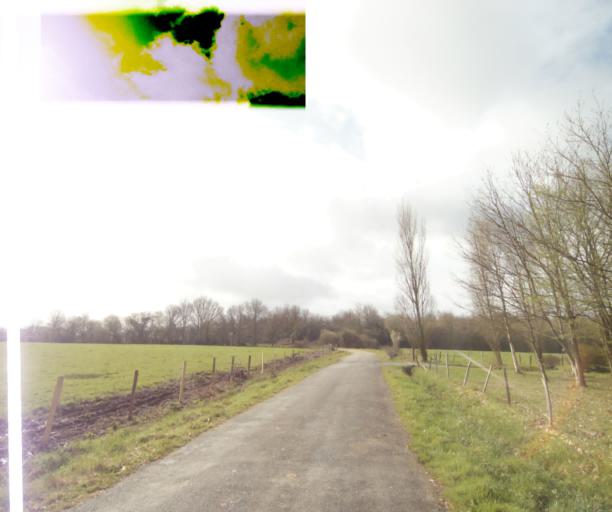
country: FR
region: Pays de la Loire
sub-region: Departement de la Loire-Atlantique
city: Bouvron
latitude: 47.4183
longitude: -1.8606
